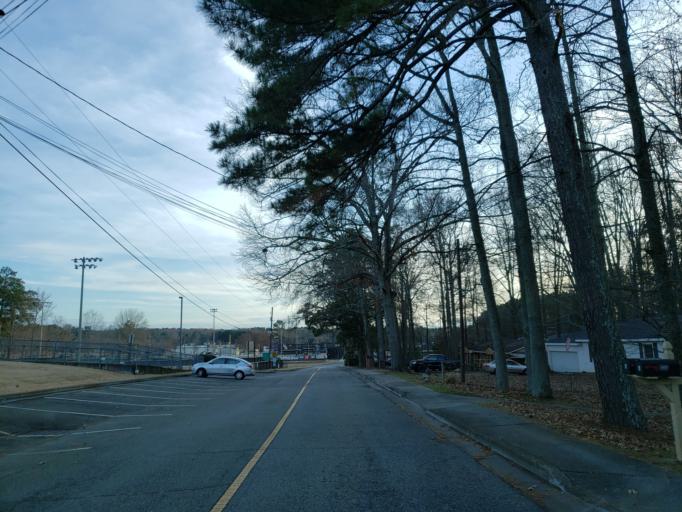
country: US
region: Georgia
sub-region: Cobb County
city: Kennesaw
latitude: 34.0248
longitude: -84.6220
